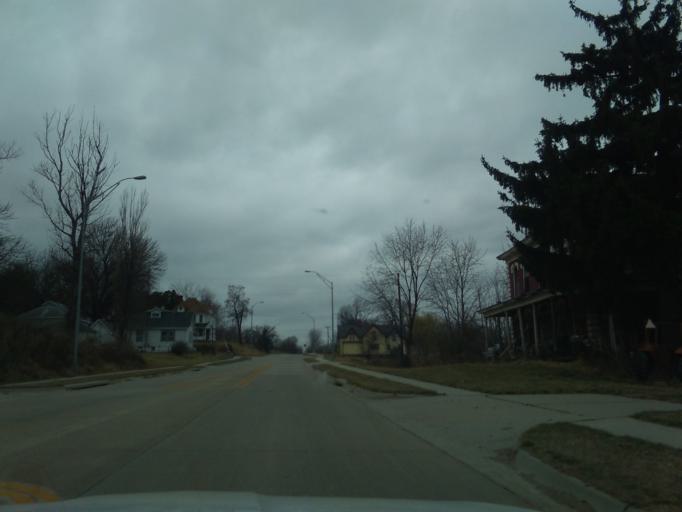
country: US
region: Nebraska
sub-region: Richardson County
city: Falls City
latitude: 40.0522
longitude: -95.4277
